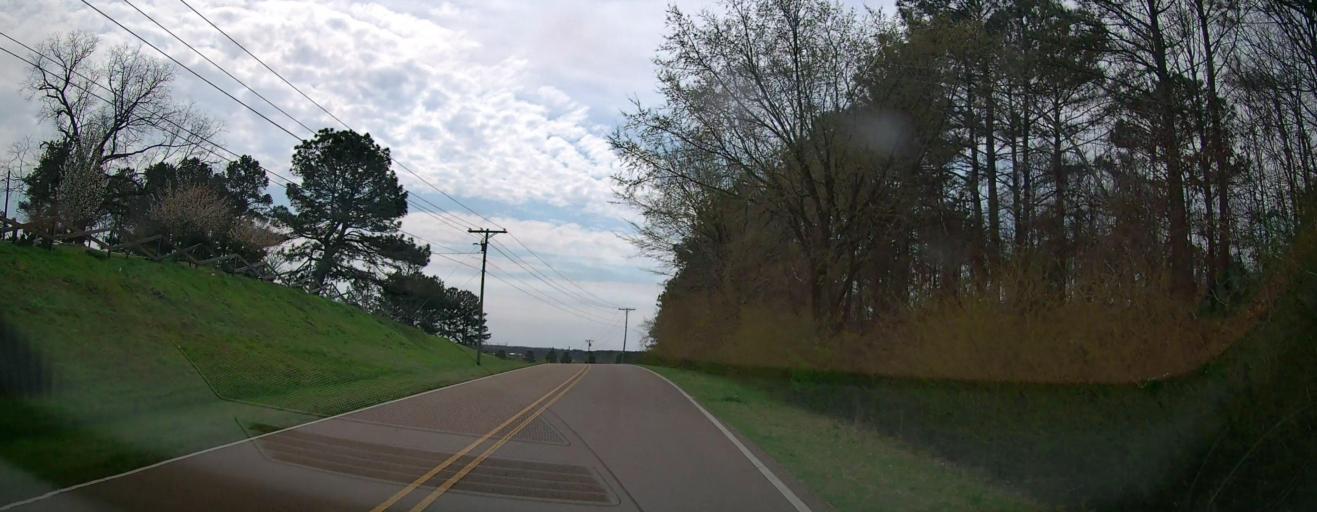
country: US
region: Mississippi
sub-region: Marshall County
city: Holly Springs
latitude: 34.7544
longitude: -89.4298
